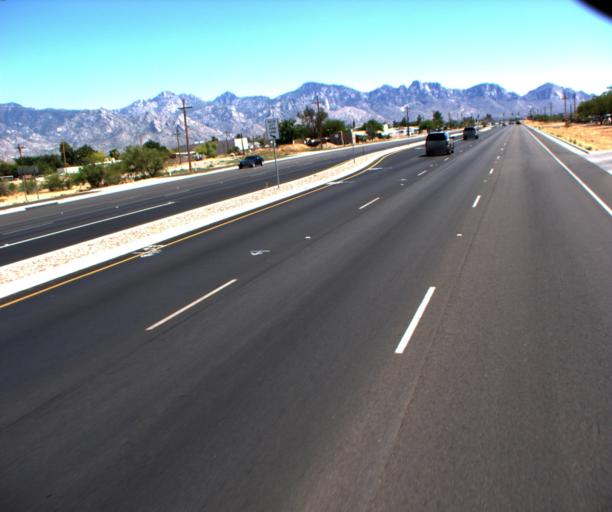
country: US
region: Arizona
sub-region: Pima County
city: Catalina
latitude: 32.5107
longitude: -110.9259
